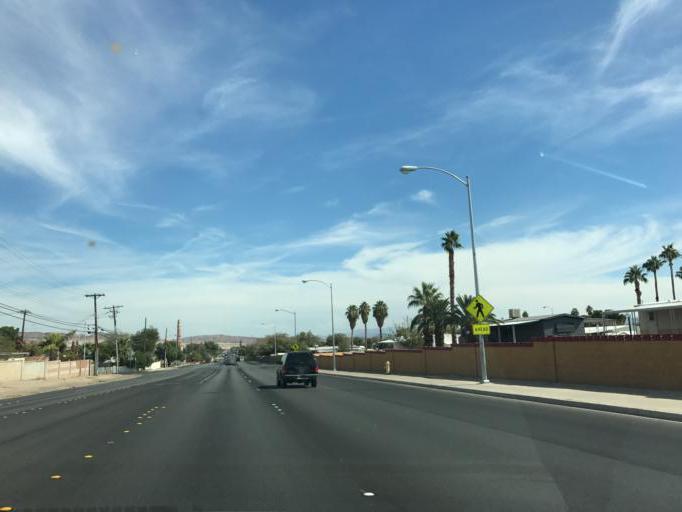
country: US
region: Nevada
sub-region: Clark County
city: Winchester
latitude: 36.1296
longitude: -115.0756
